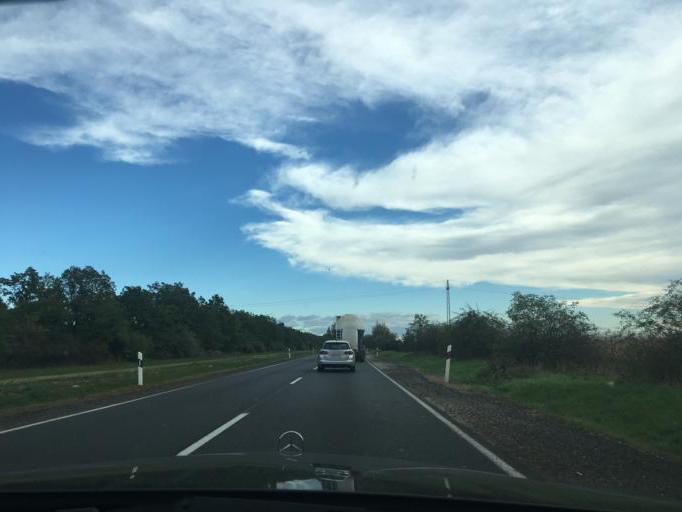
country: HU
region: Borsod-Abauj-Zemplen
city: Arnot
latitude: 48.1190
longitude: 20.8653
